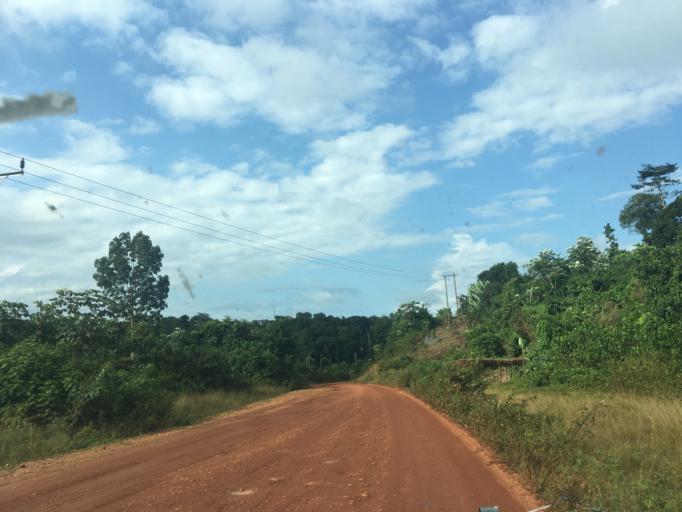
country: GH
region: Western
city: Wassa-Akropong
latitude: 5.9596
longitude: -2.4291
